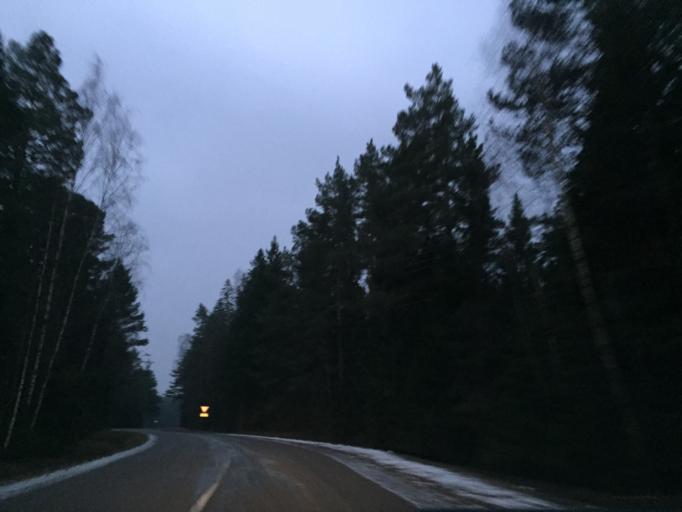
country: EE
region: Saare
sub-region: Kuressaare linn
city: Kuressaare
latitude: 58.5934
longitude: 22.6070
